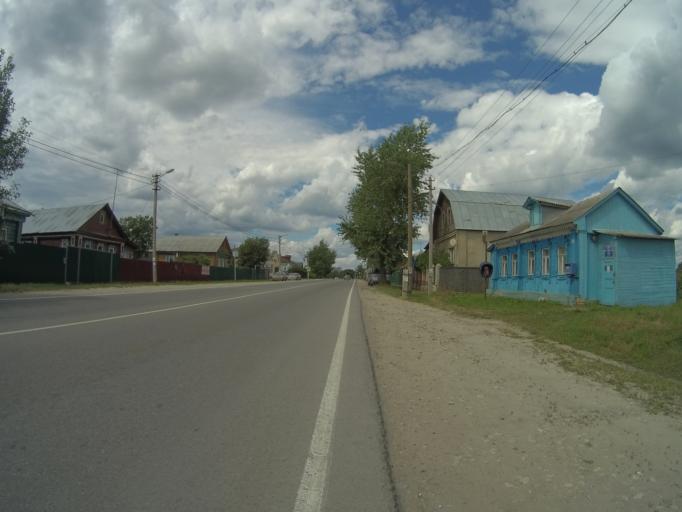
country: RU
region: Vladimir
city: Kommunar
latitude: 56.0418
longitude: 40.5462
